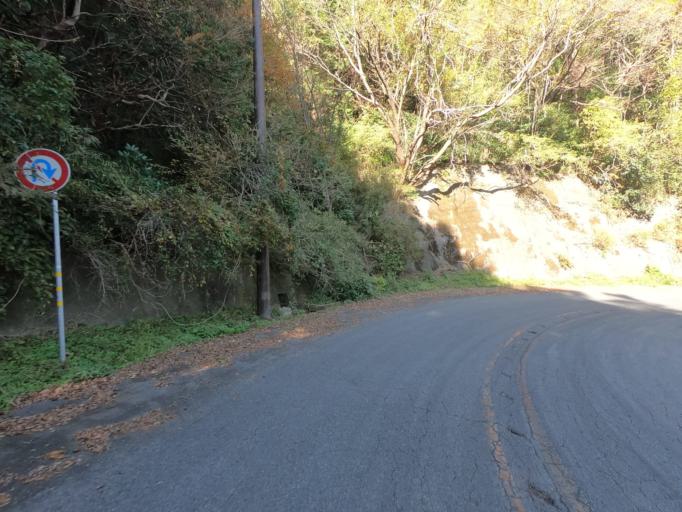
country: JP
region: Ibaraki
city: Tsukuba
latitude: 36.2160
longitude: 140.1232
